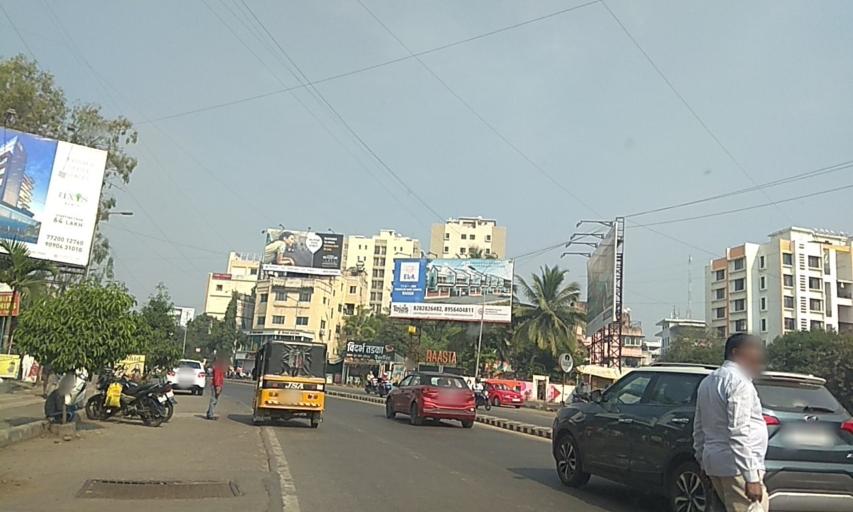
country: IN
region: Maharashtra
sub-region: Pune Division
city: Pimpri
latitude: 18.5624
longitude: 73.7838
